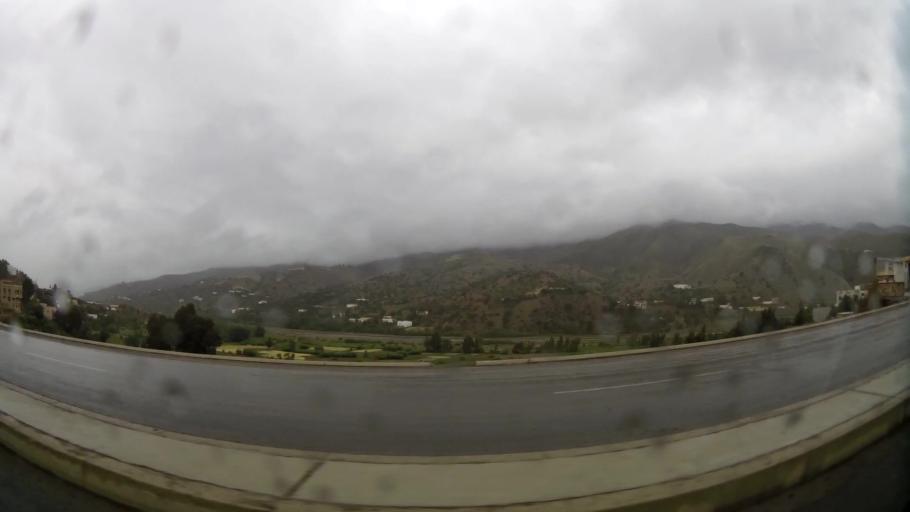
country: MA
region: Taza-Al Hoceima-Taounate
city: Imzourene
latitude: 35.0234
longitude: -3.8222
